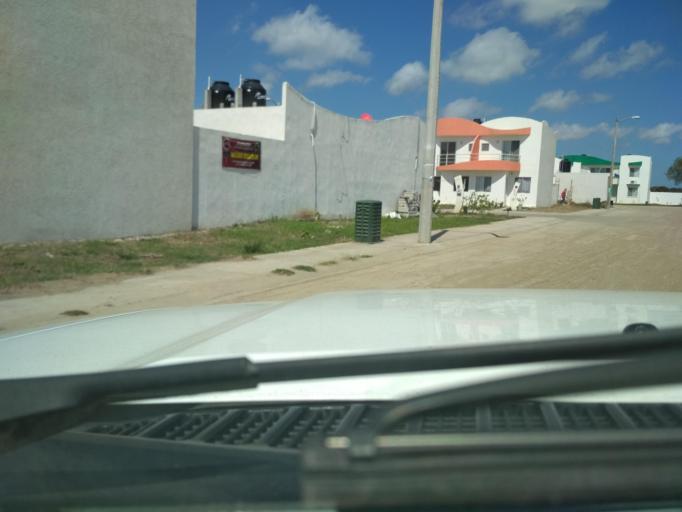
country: MX
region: Veracruz
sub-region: Veracruz
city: Las Amapolas
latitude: 19.1330
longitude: -96.2028
